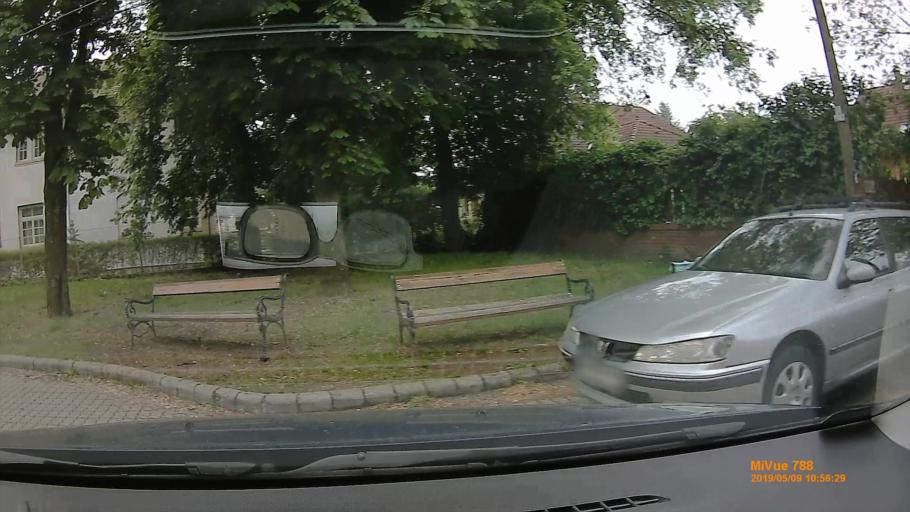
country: HU
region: Budapest
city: Budapest XVI. keruelet
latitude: 47.5212
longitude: 19.1614
